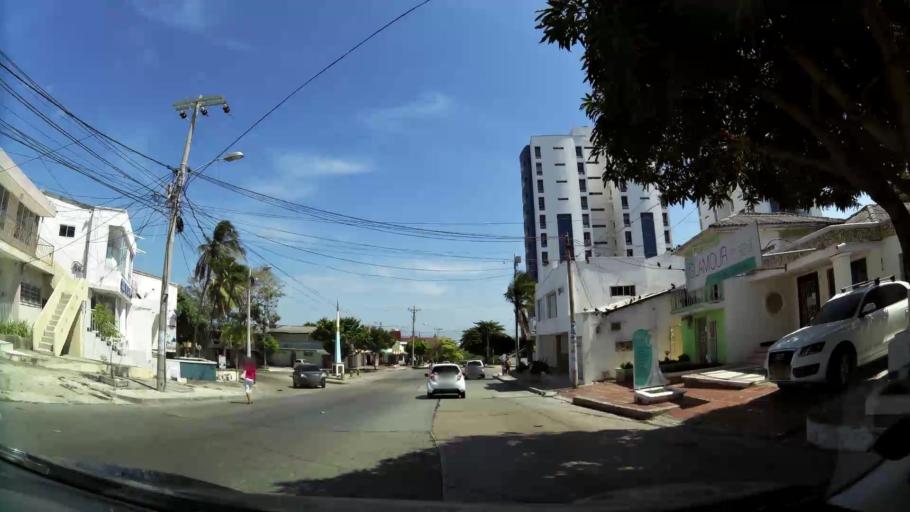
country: CO
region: Atlantico
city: Barranquilla
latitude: 10.9838
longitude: -74.8052
